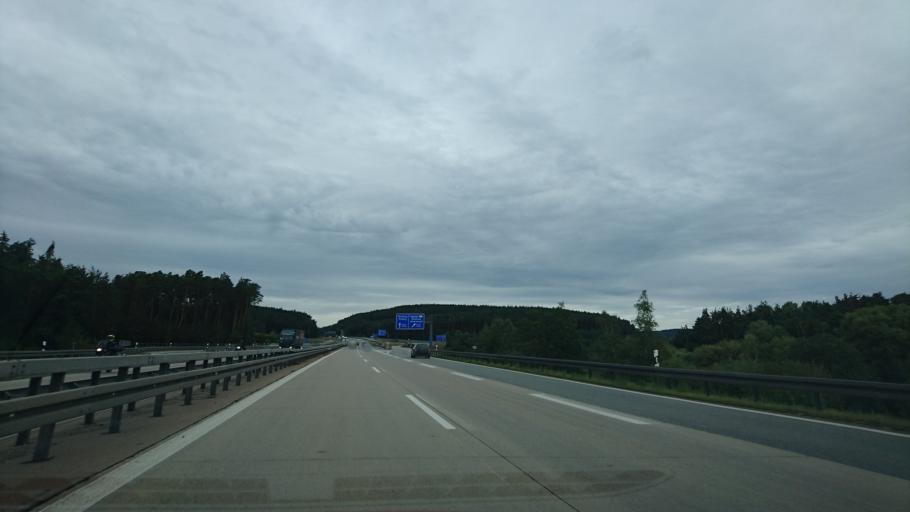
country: DE
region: Bavaria
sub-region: Upper Palatinate
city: Wernberg-Koblitz
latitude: 49.5146
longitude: 12.1682
